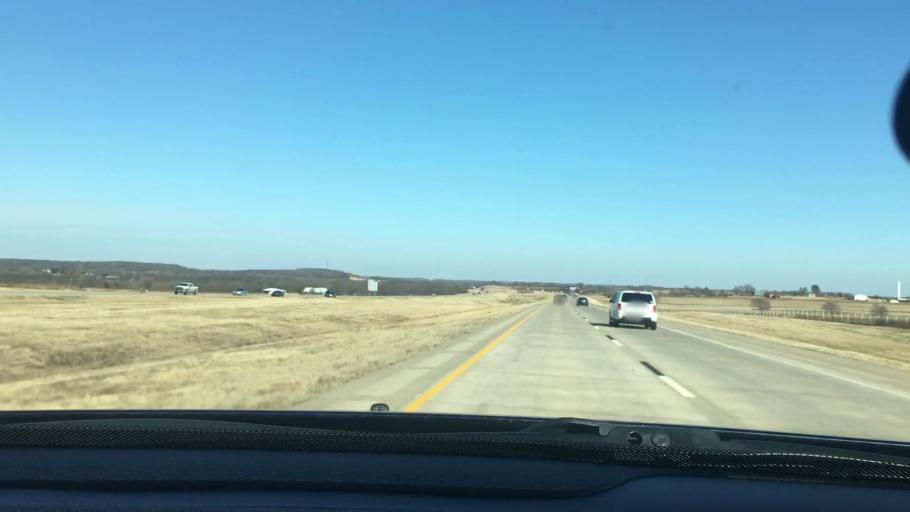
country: US
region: Oklahoma
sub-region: Love County
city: Marietta
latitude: 33.9679
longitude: -97.1341
